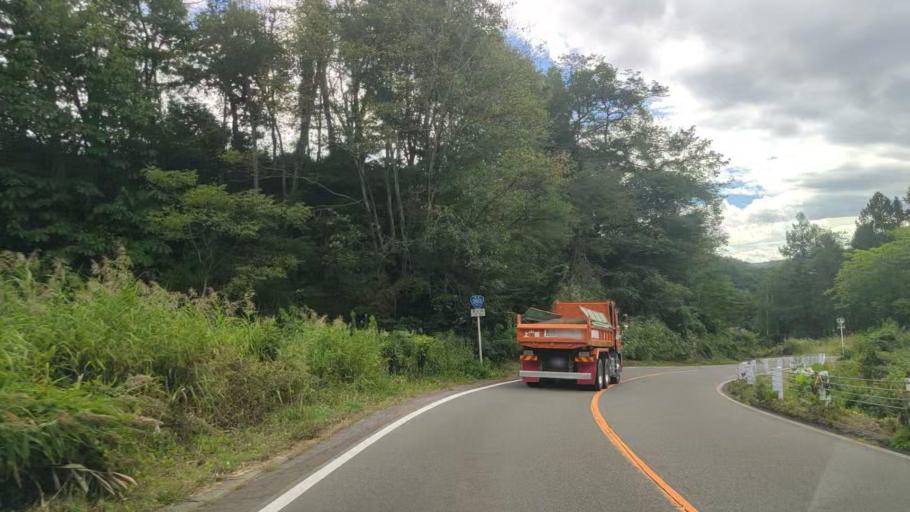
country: JP
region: Nagano
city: Iiyama
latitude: 36.8745
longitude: 138.3207
